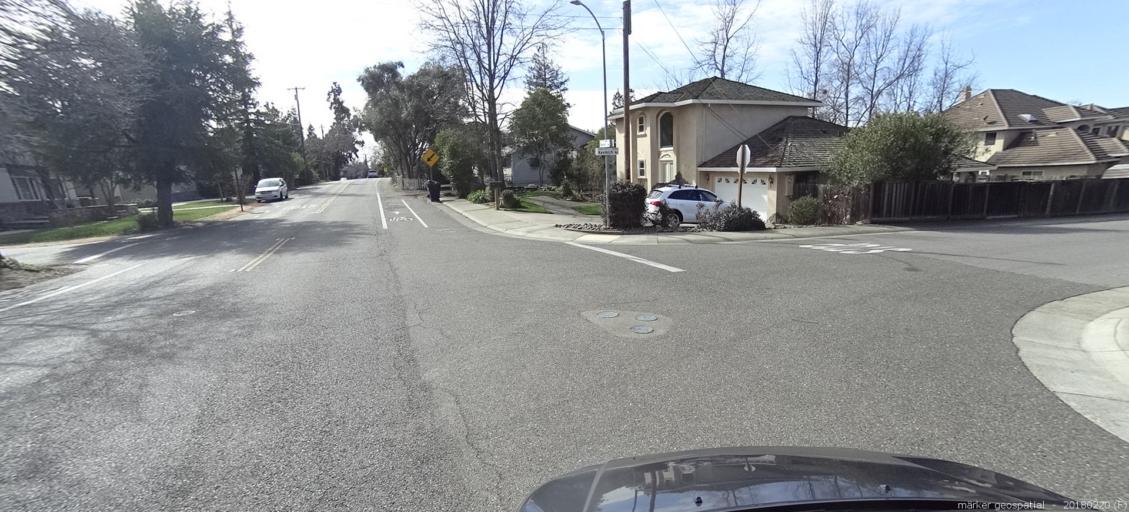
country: US
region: California
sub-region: Sacramento County
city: Orangevale
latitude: 38.6746
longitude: -121.2304
